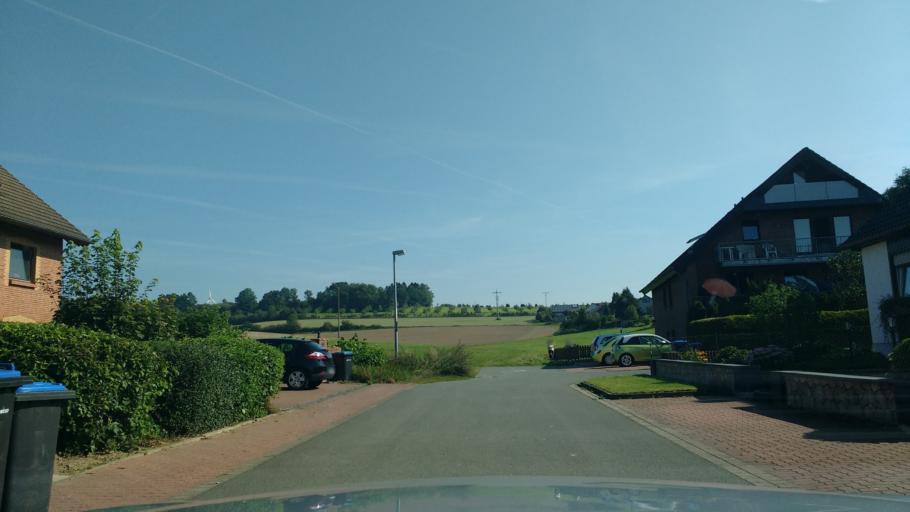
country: DE
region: North Rhine-Westphalia
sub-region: Regierungsbezirk Detmold
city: Dorentrup
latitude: 52.0291
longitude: 9.0545
